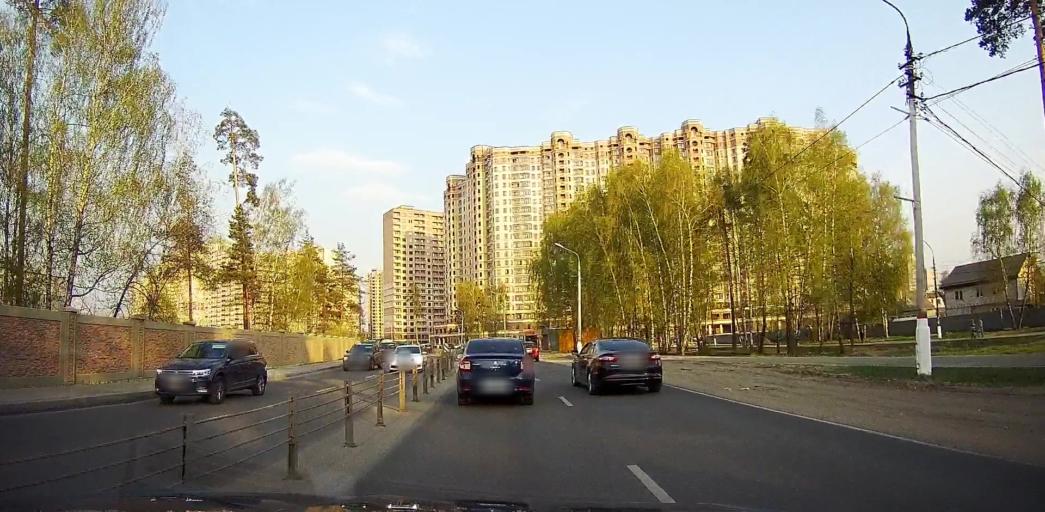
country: RU
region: Moskovskaya
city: Ramenskoye
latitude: 55.5821
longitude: 38.2098
